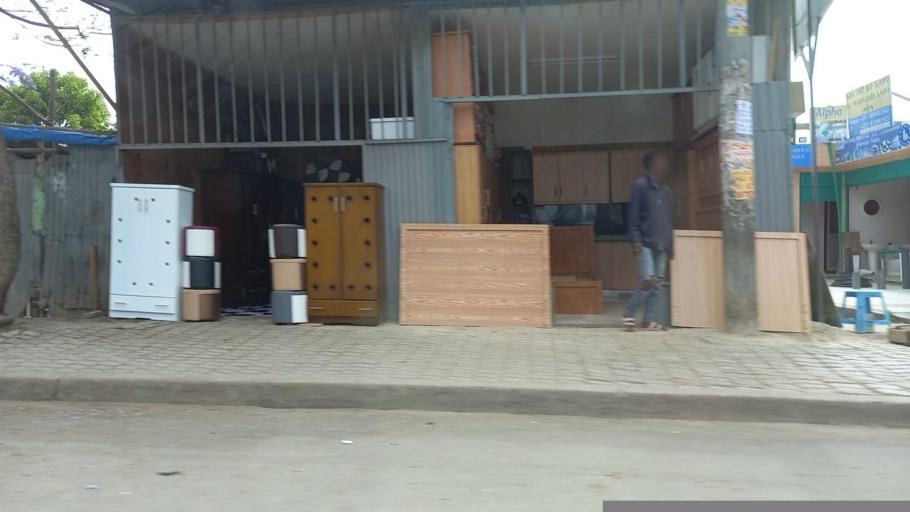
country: ET
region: Adis Abeba
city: Addis Ababa
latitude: 9.0220
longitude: 38.7872
